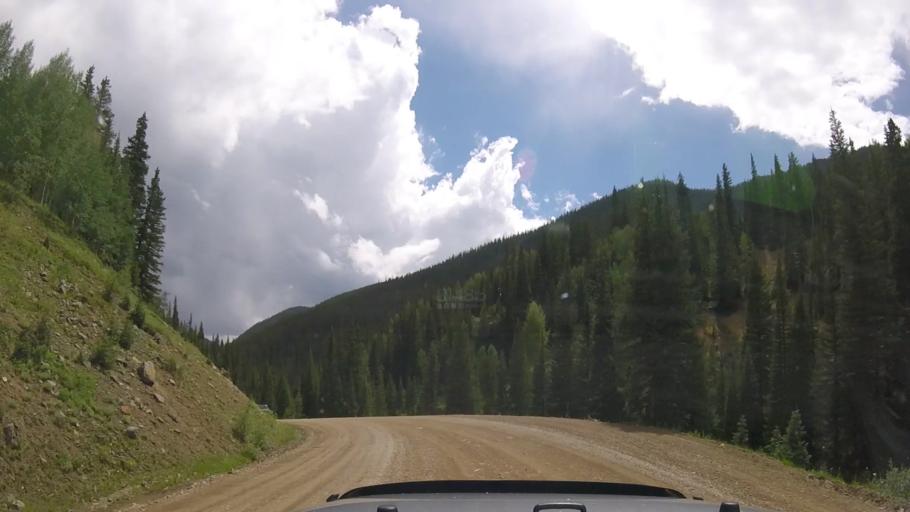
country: US
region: Colorado
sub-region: San Juan County
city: Silverton
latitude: 37.8386
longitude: -107.6787
